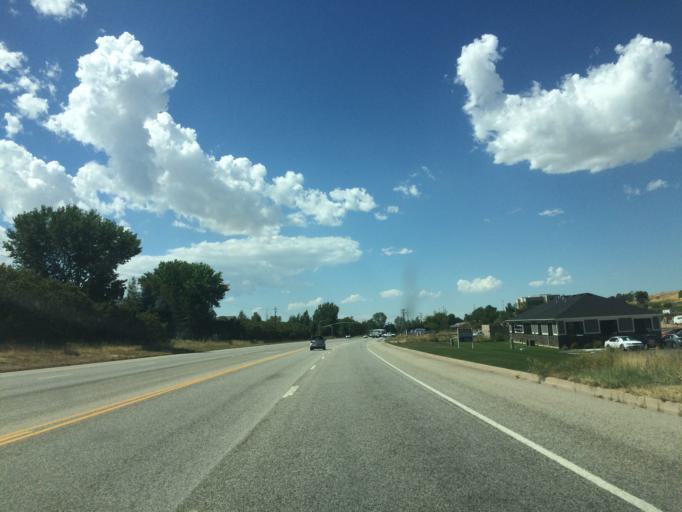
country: US
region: Utah
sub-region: Davis County
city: South Weber
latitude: 41.1028
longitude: -111.9298
